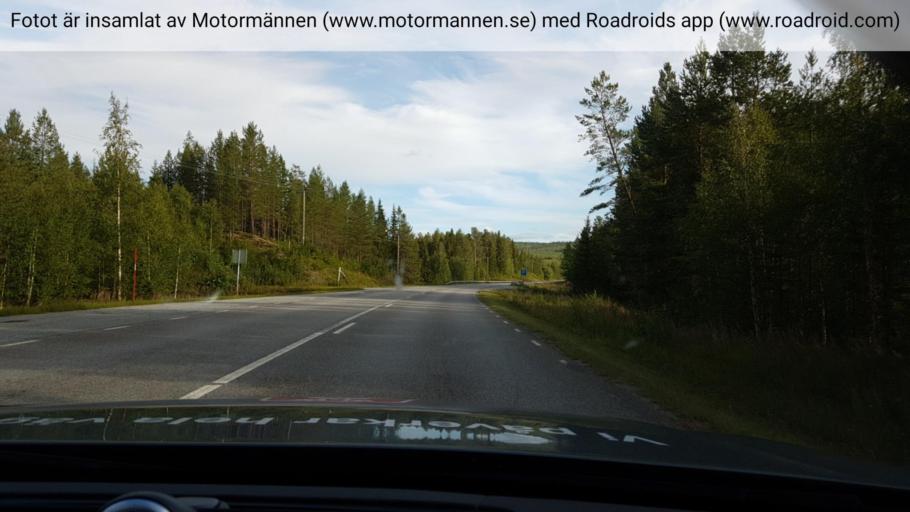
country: SE
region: Jaemtland
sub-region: Stroemsunds Kommun
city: Stroemsund
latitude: 64.2468
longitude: 15.4473
